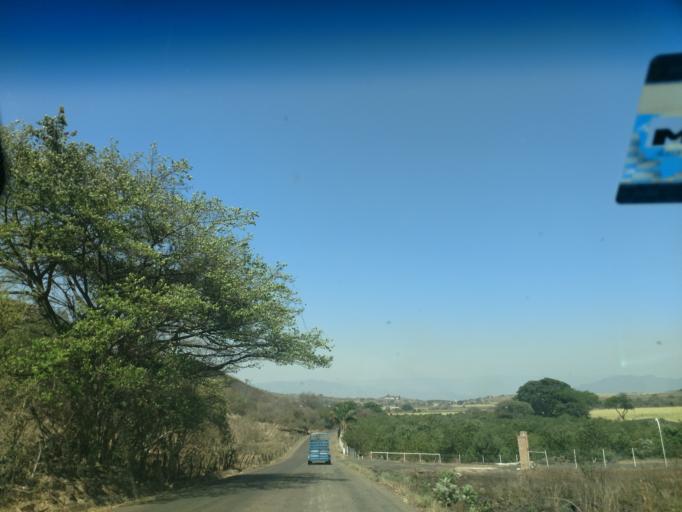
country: MX
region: Nayarit
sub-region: Tepic
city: La Corregidora
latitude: 21.5040
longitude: -104.7296
